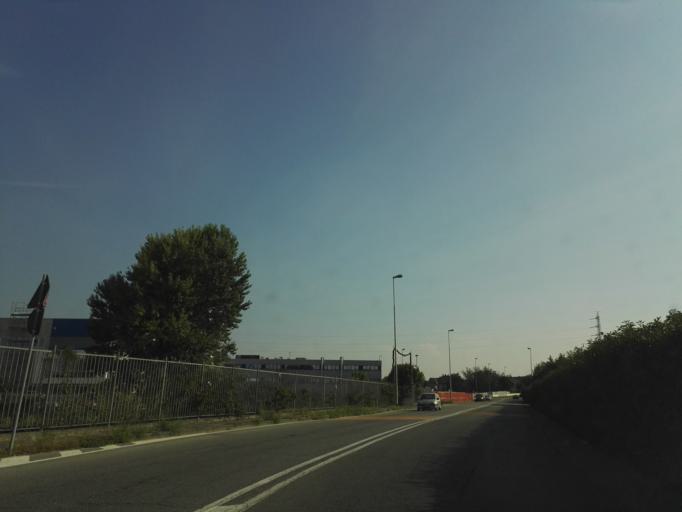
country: IT
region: Lombardy
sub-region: Citta metropolitana di Milano
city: Triginto
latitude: 45.3881
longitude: 9.3084
